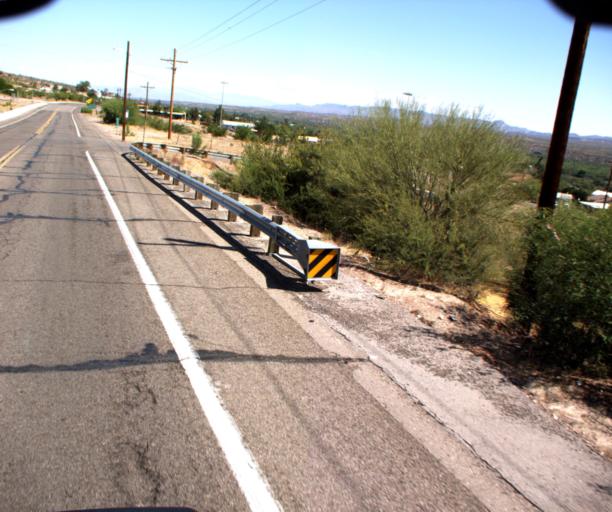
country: US
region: Arizona
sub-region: Pinal County
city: Mammoth
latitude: 32.7169
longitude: -110.6425
